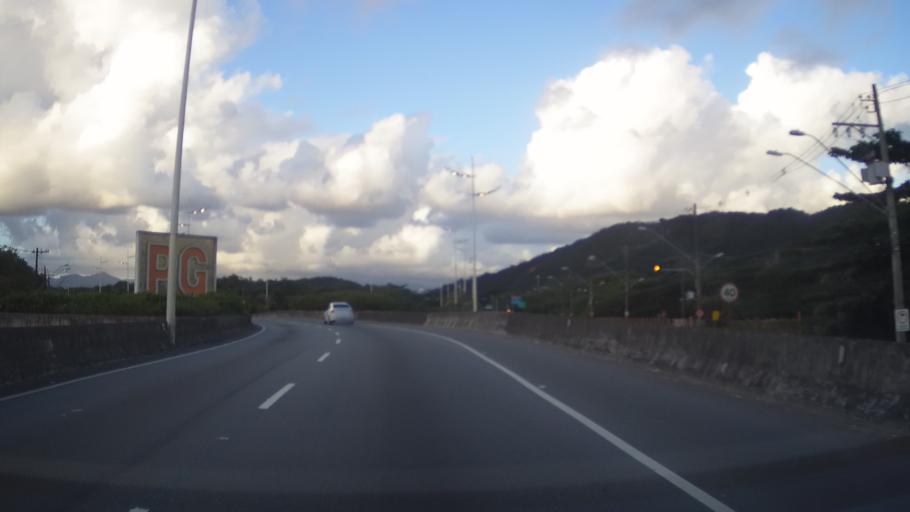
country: BR
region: Sao Paulo
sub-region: Praia Grande
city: Praia Grande
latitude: -23.9902
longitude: -46.4012
